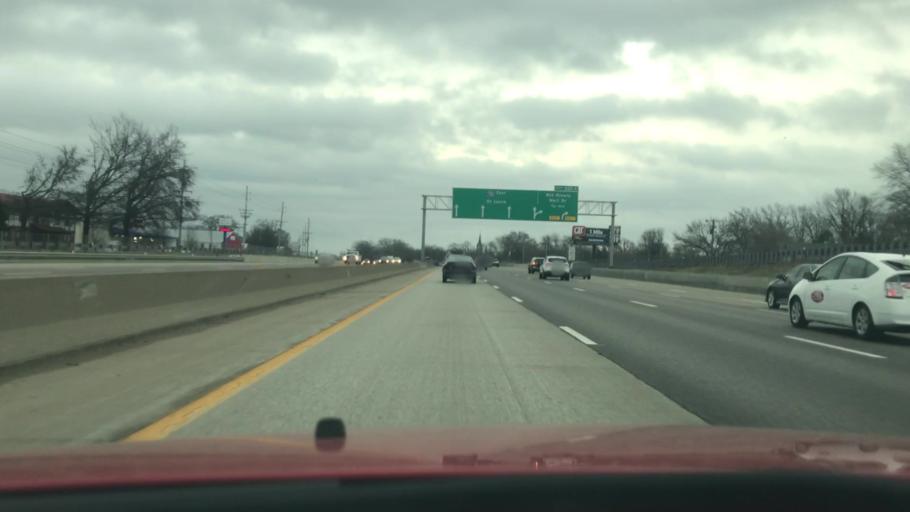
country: US
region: Missouri
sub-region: Saint Charles County
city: Saint Peters
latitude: 38.7999
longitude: -90.6409
